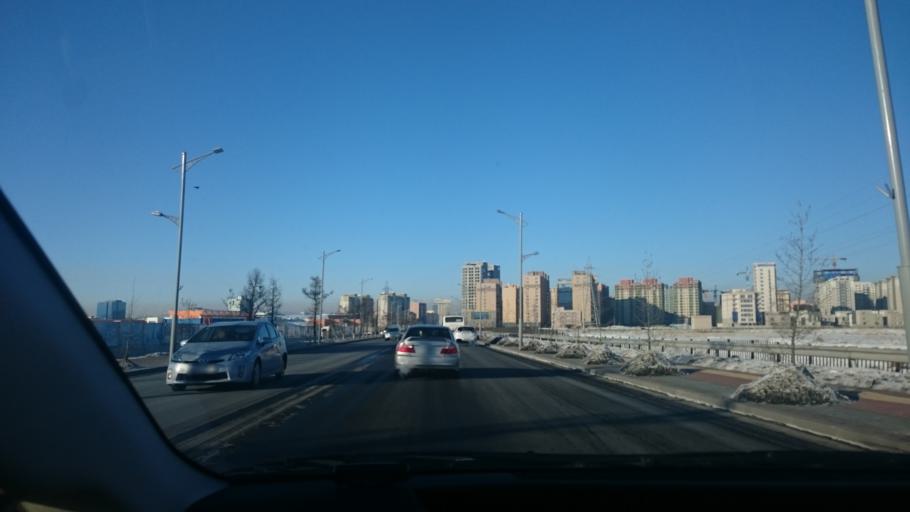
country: MN
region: Ulaanbaatar
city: Ulaanbaatar
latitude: 47.8961
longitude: 106.9340
